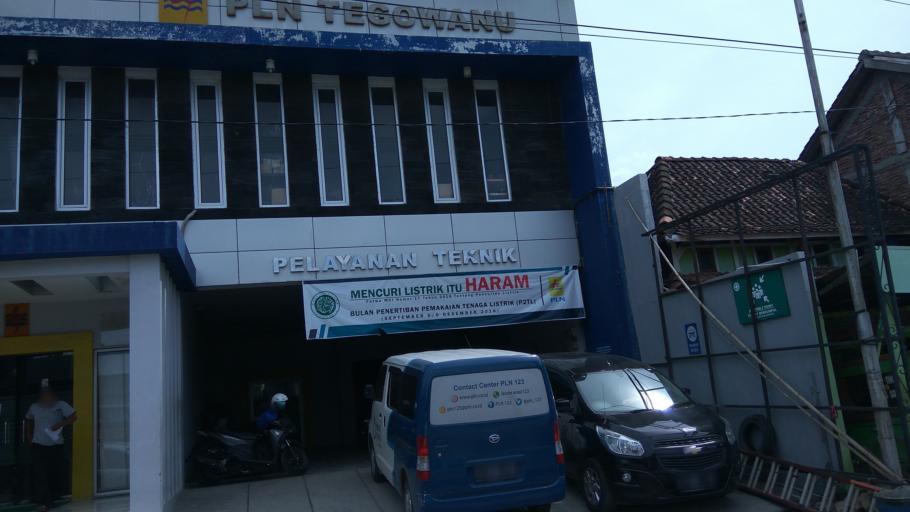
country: ID
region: Central Java
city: Mranggen
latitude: -7.0499
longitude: 110.6034
